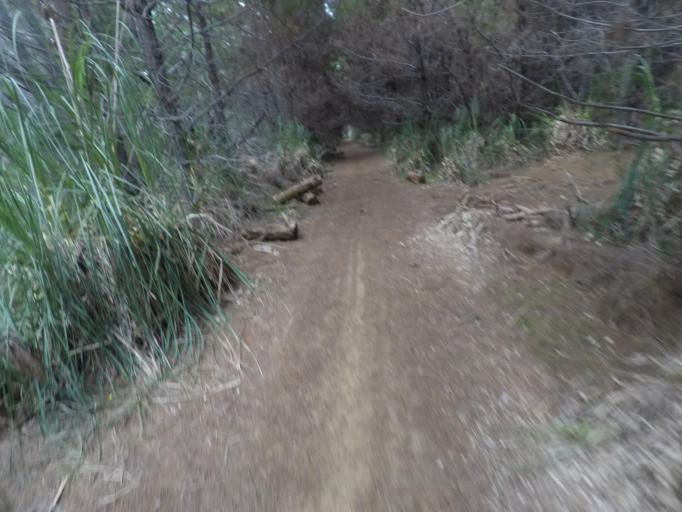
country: NZ
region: Auckland
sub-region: Auckland
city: Parakai
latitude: -36.6032
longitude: 174.2727
